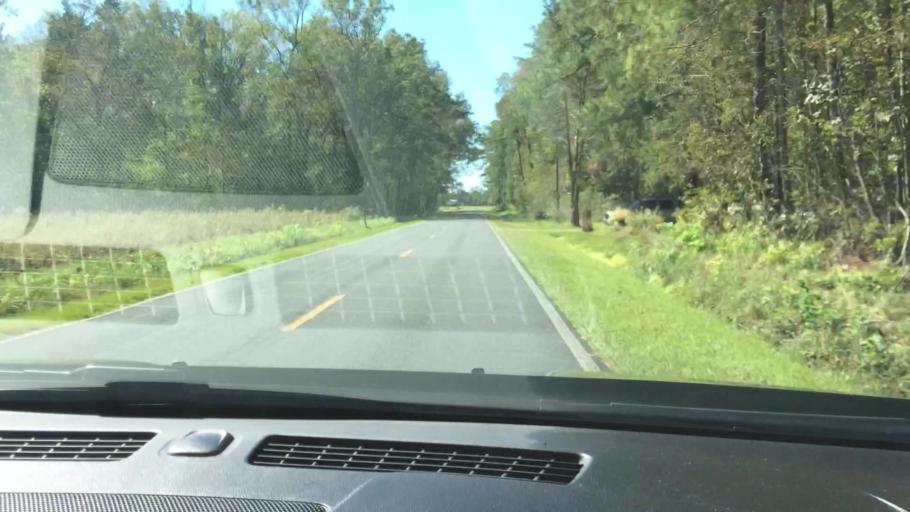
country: US
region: North Carolina
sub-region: Pitt County
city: Grifton
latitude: 35.3018
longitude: -77.3199
